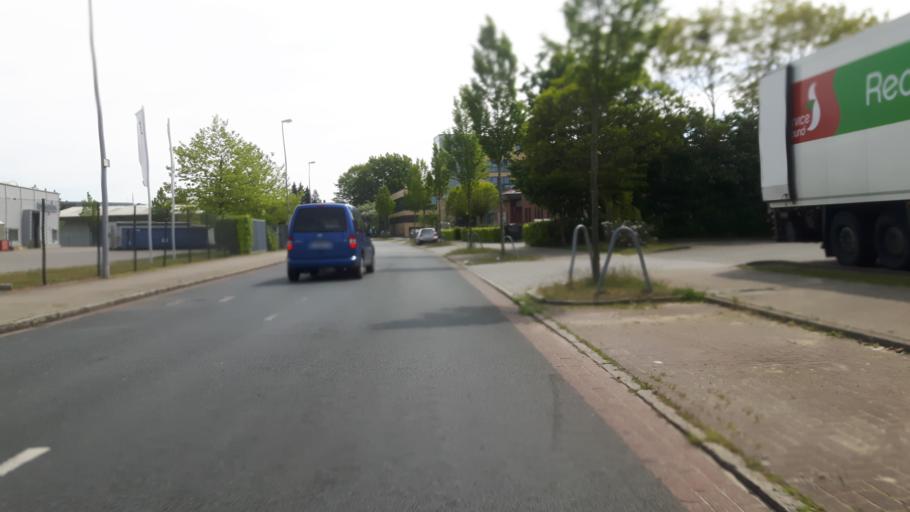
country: DE
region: Lower Saxony
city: Stuhr
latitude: 53.0583
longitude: 8.7747
